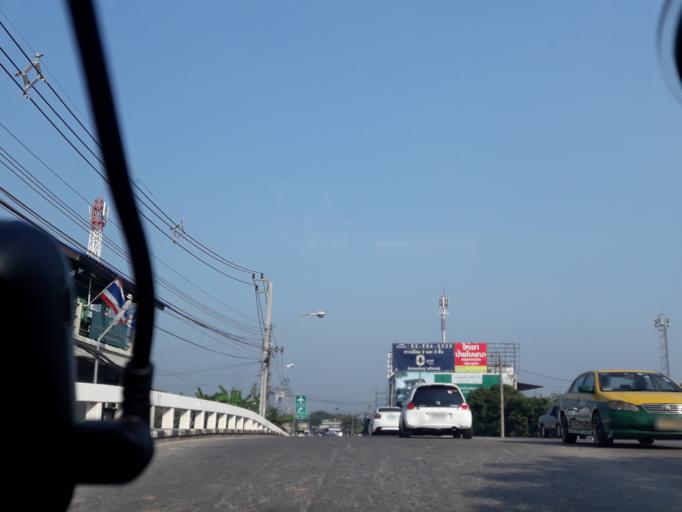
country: TH
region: Bangkok
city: Khlong Sam Wa
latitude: 13.8595
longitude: 100.7290
